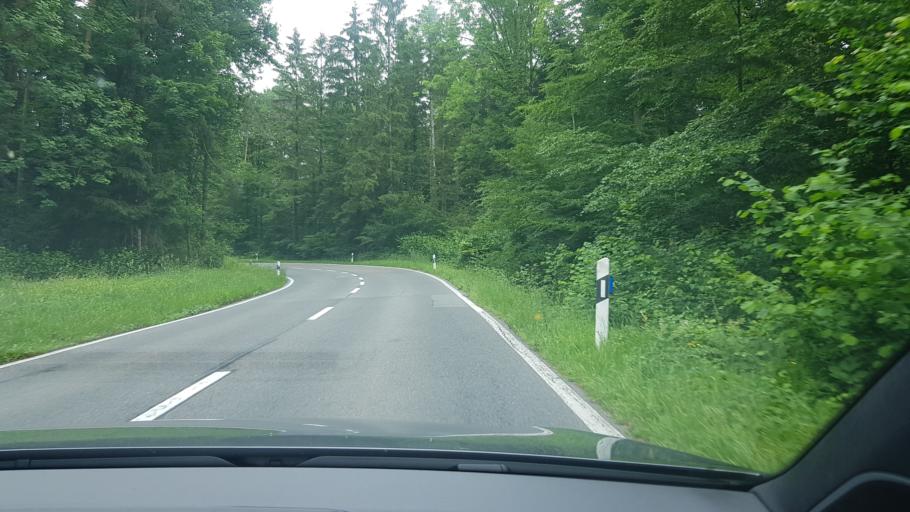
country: CH
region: Zug
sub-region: Zug
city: Baar
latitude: 47.1948
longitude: 8.5463
